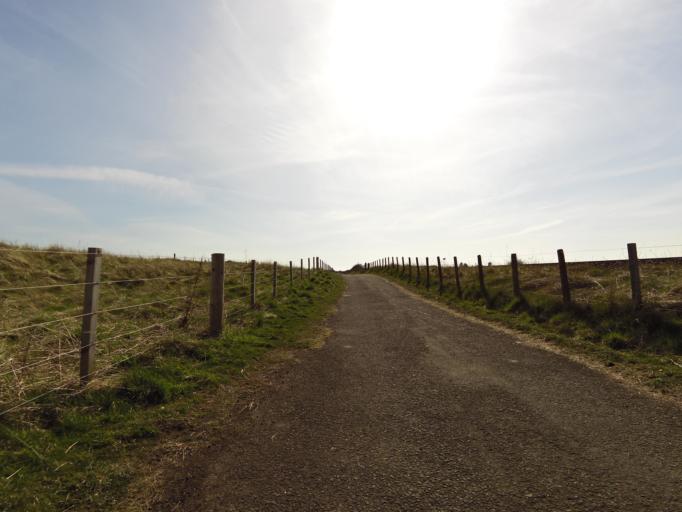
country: GB
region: Scotland
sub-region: Angus
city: Arbroath
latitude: 56.5370
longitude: -2.6280
